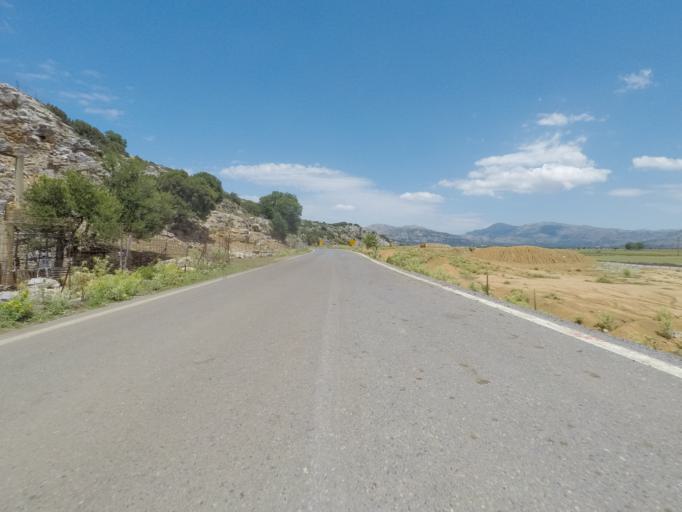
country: GR
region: Crete
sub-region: Nomos Irakleiou
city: Mokhos
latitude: 35.1937
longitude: 25.4388
